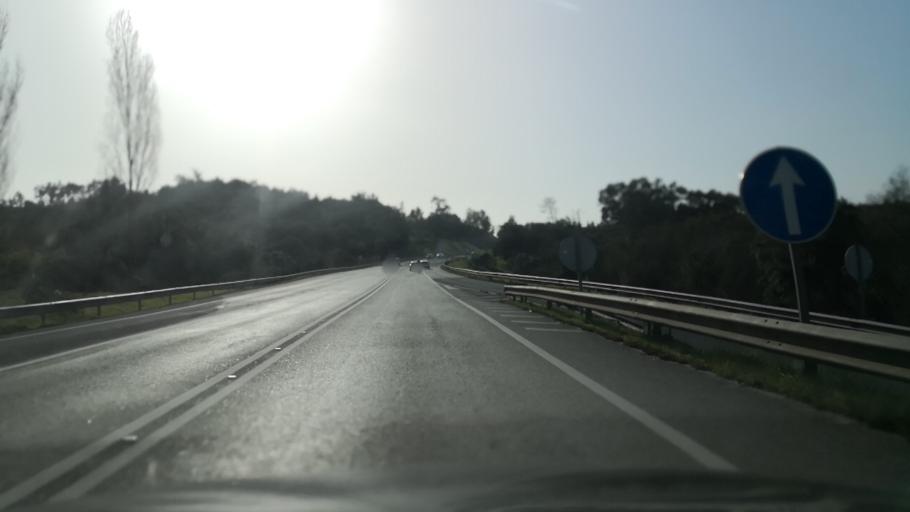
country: PT
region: Leiria
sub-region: Leiria
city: Leiria
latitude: 39.7460
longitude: -8.8286
